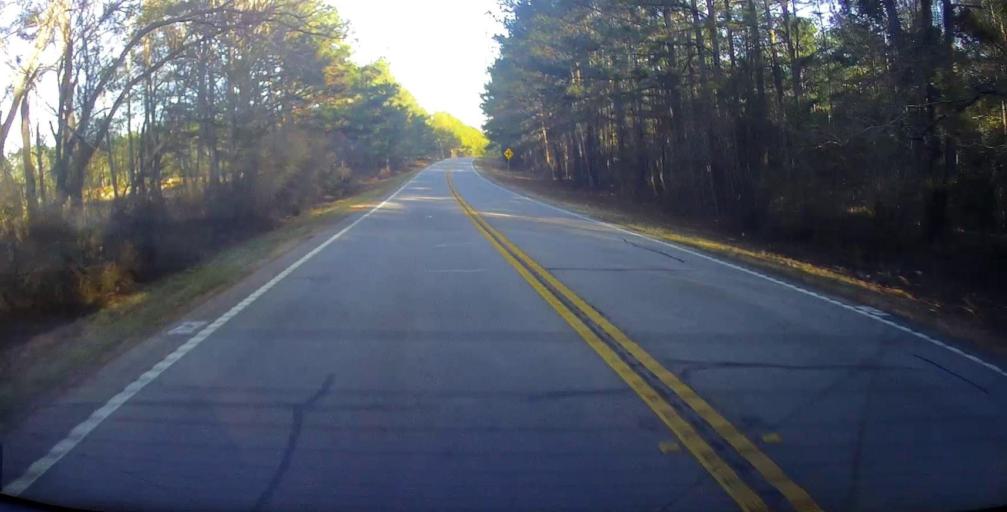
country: US
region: Georgia
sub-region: Harris County
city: Pine Mountain
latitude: 32.8553
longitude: -84.9456
